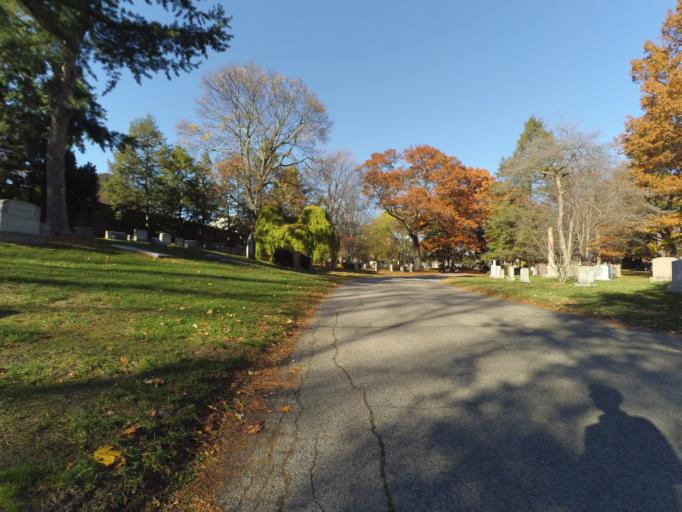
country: US
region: Massachusetts
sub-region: Middlesex County
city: Watertown
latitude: 42.3724
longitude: -71.1490
